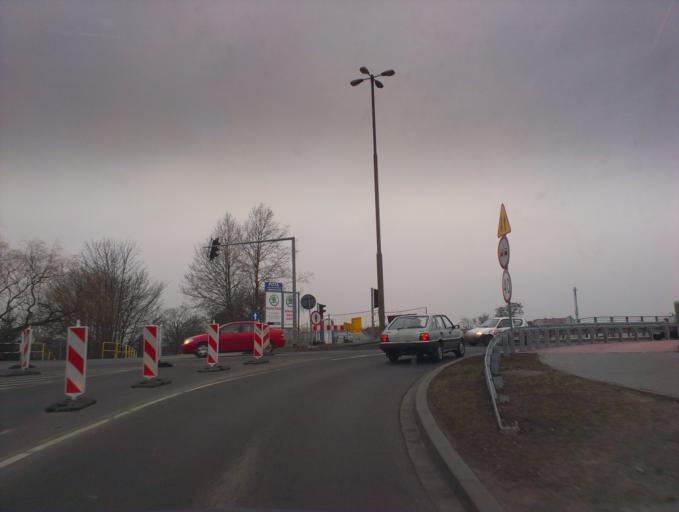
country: PL
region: Greater Poland Voivodeship
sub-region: Powiat pilski
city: Pila
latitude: 53.1423
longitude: 16.7407
